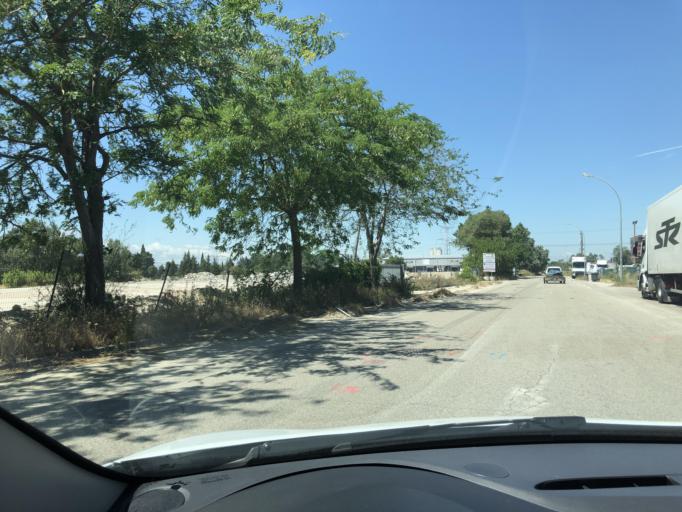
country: FR
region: Provence-Alpes-Cote d'Azur
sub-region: Departement des Bouches-du-Rhone
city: Chateaurenard
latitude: 43.8976
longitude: 4.8749
